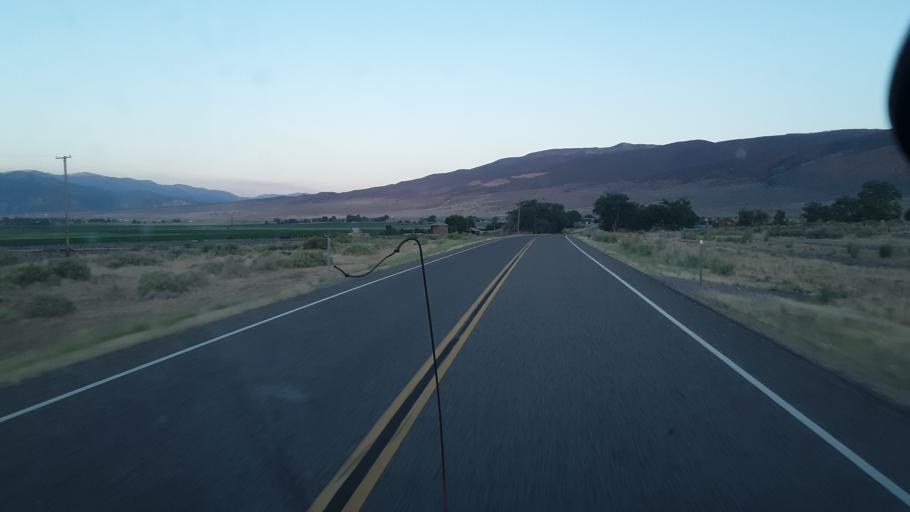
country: US
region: Utah
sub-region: Sevier County
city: Monroe
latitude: 38.6547
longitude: -112.1901
